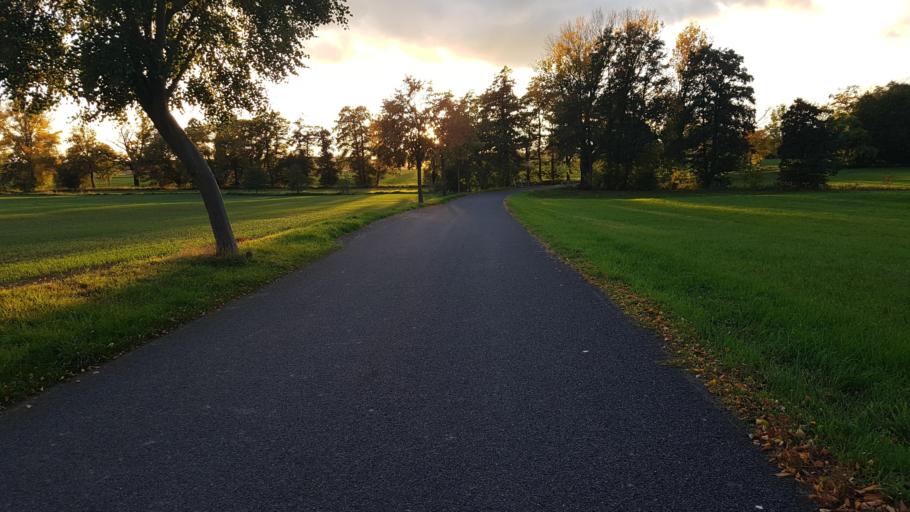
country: DE
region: Saxony
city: Priestewitz
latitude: 51.2316
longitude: 13.5424
